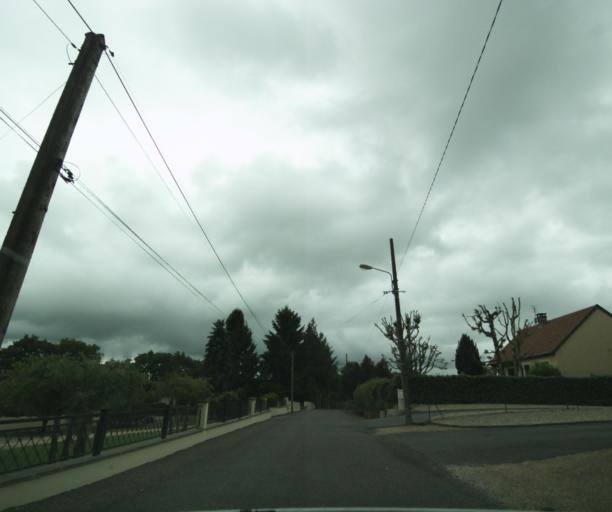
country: FR
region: Bourgogne
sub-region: Departement de Saone-et-Loire
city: Charolles
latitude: 46.4426
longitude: 4.2805
